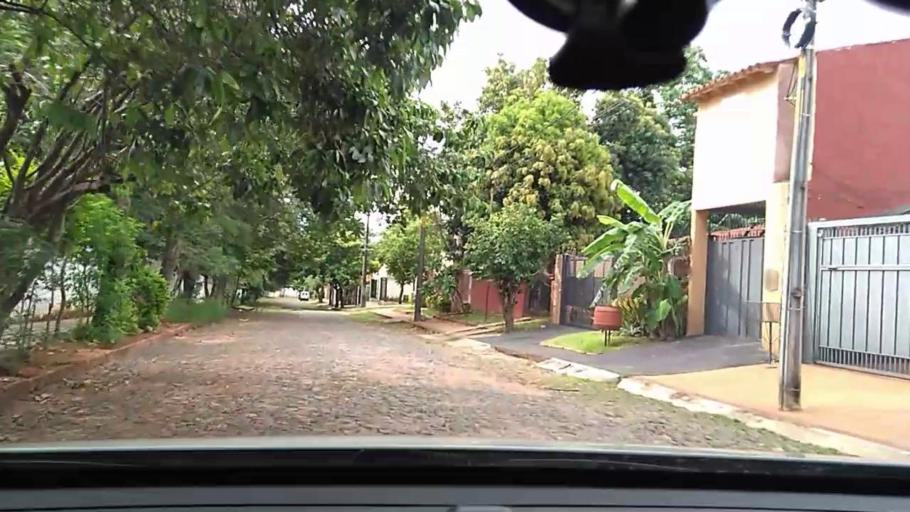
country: PY
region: Asuncion
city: Asuncion
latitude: -25.2702
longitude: -57.5791
